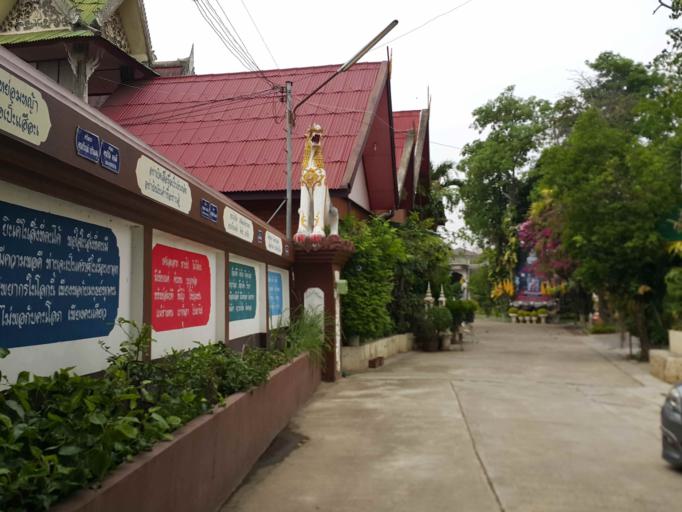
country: TH
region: Chiang Mai
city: Saraphi
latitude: 18.7538
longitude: 99.0186
